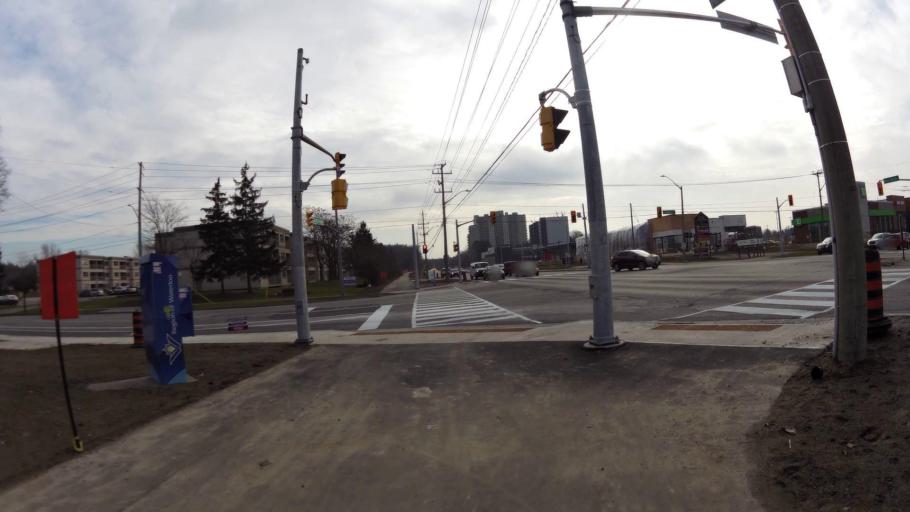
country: CA
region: Ontario
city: Kitchener
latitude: 43.3956
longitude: -80.4319
